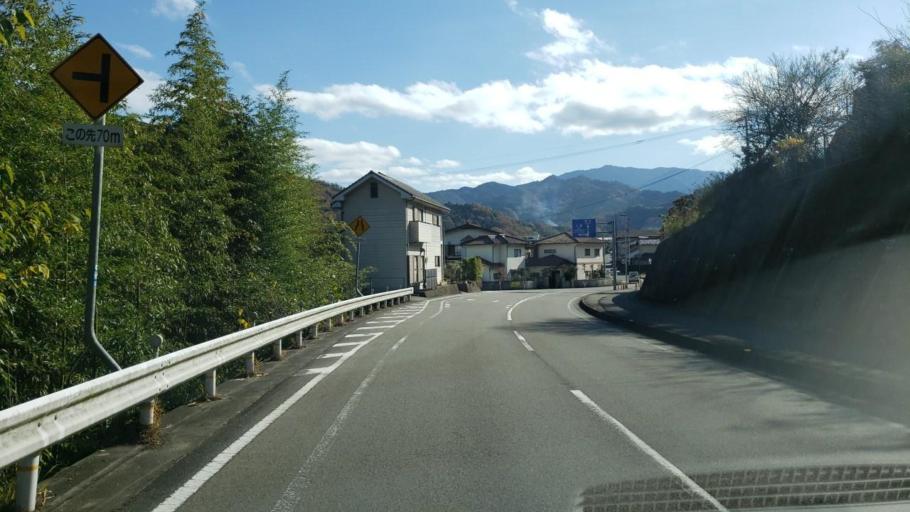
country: JP
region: Tokushima
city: Wakimachi
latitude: 34.0376
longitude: 134.0277
